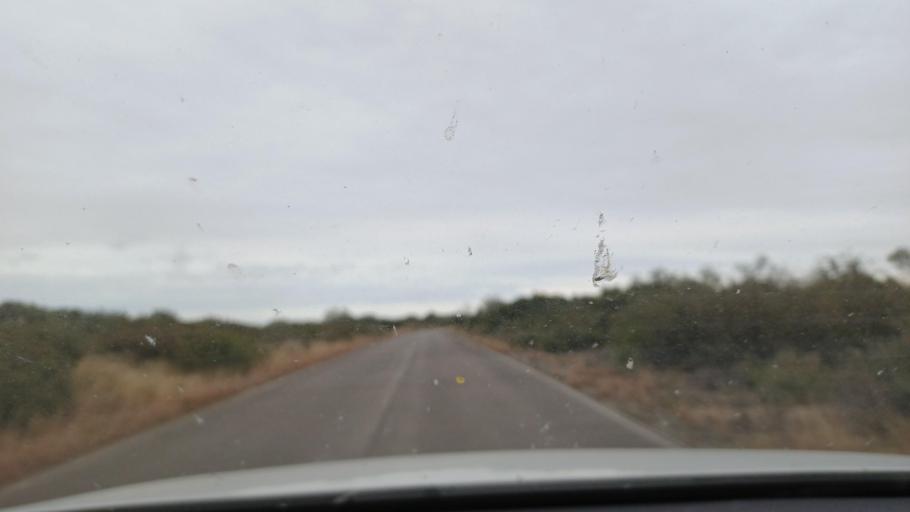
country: ES
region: Valencia
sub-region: Provincia de Castello
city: Canet lo Roig
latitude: 40.5879
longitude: 0.2839
